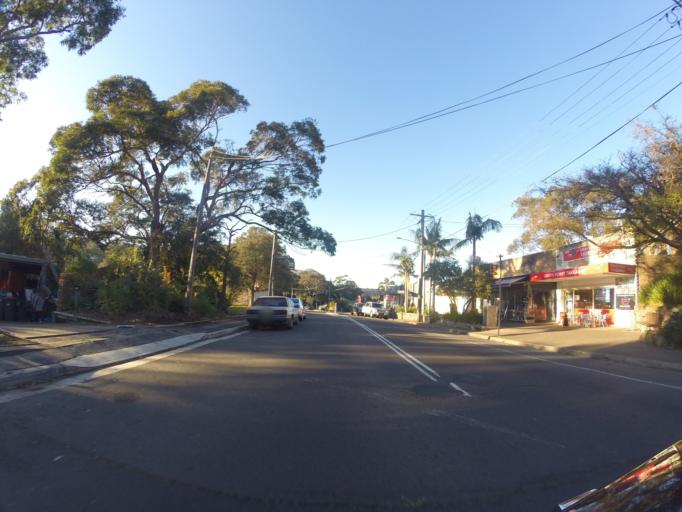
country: AU
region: New South Wales
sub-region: Sutherland Shire
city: Grays Point
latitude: -34.0584
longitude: 151.0812
